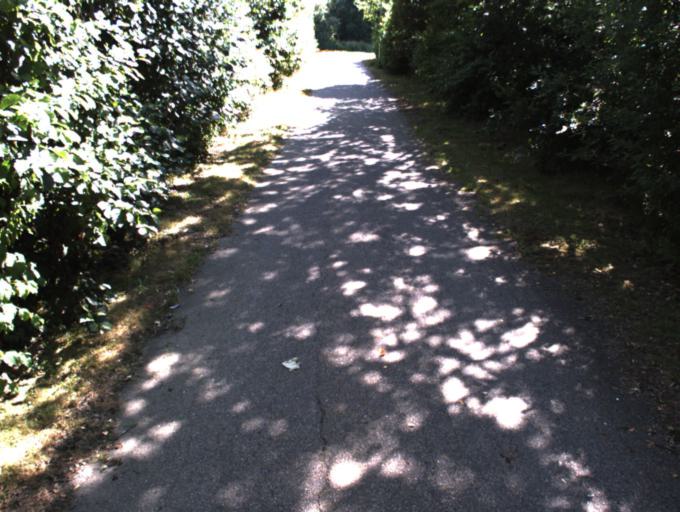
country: SE
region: Skane
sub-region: Helsingborg
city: Odakra
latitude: 56.0805
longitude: 12.7376
